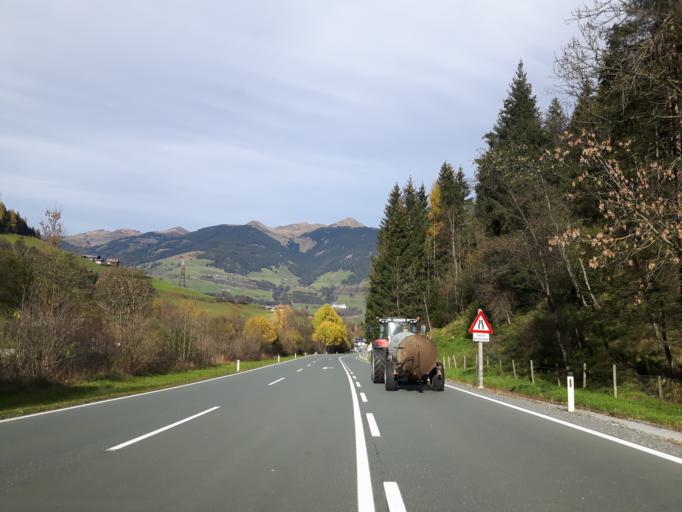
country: AT
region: Salzburg
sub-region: Politischer Bezirk Zell am See
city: Mittersill
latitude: 47.2620
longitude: 12.4846
